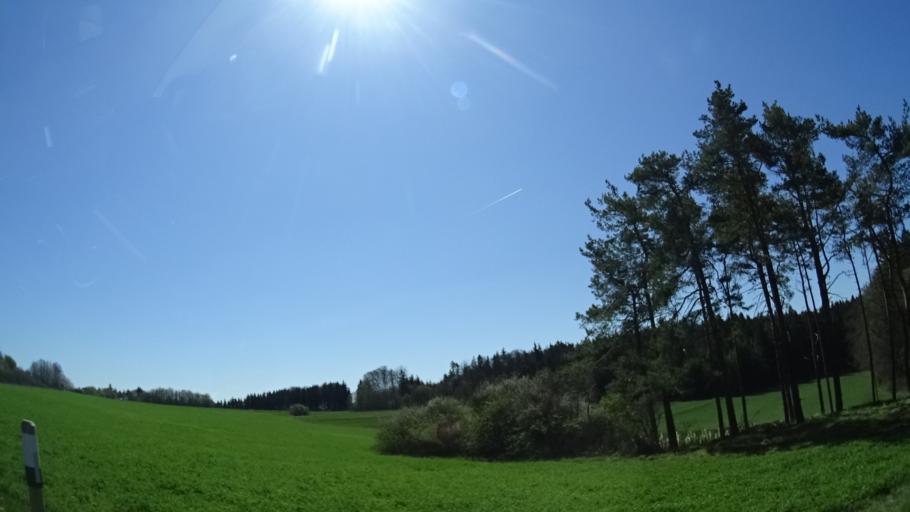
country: DE
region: Bavaria
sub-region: Regierungsbezirk Mittelfranken
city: Alfeld
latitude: 49.4099
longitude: 11.5848
